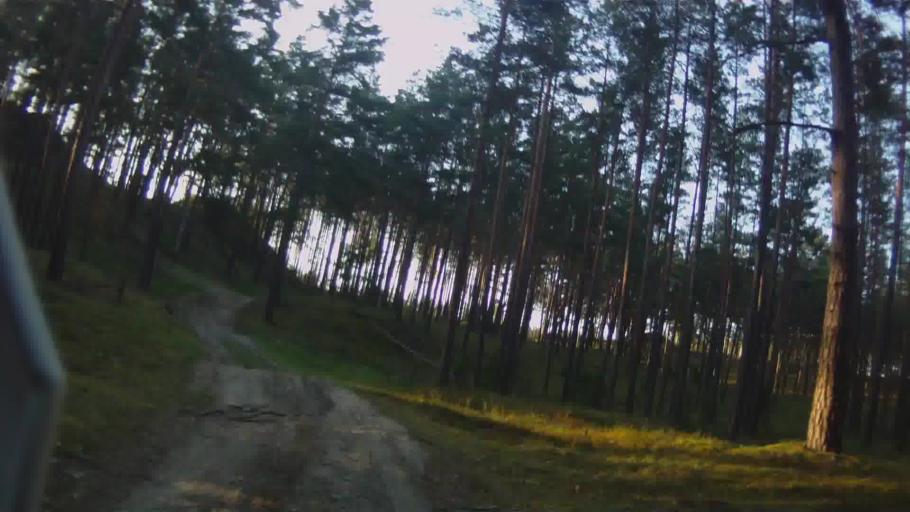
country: LV
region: Riga
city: Jaunciems
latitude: 57.0653
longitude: 24.1803
